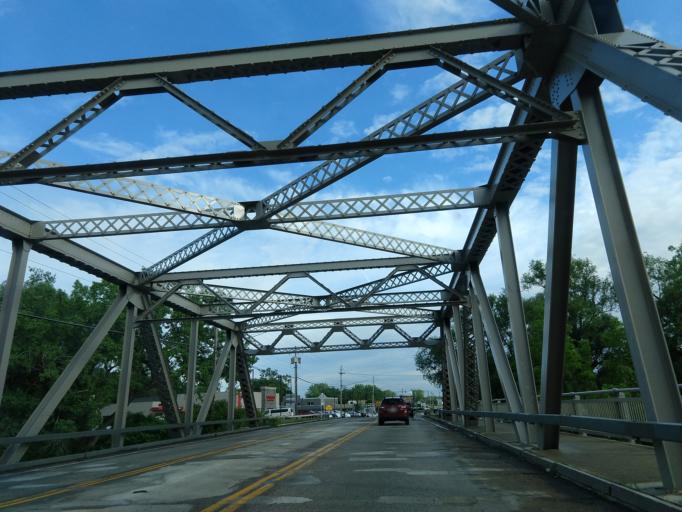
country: US
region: New York
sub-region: Erie County
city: West Seneca
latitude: 42.8416
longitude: -78.7895
